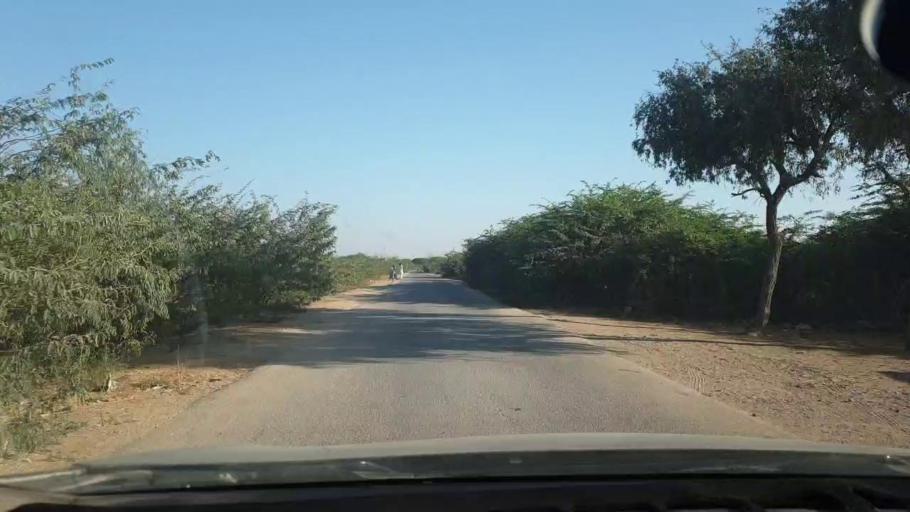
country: PK
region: Sindh
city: Malir Cantonment
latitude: 25.1452
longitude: 67.1869
